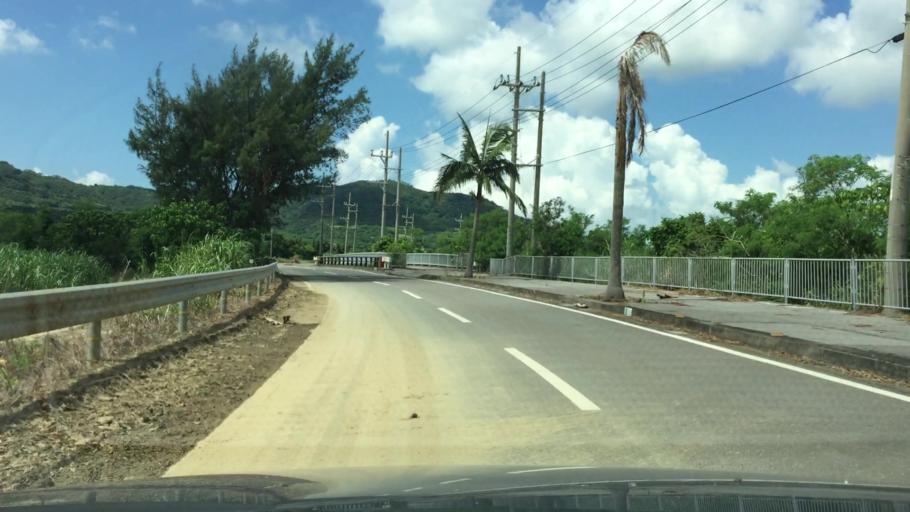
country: JP
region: Okinawa
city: Ishigaki
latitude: 24.3916
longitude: 124.1511
